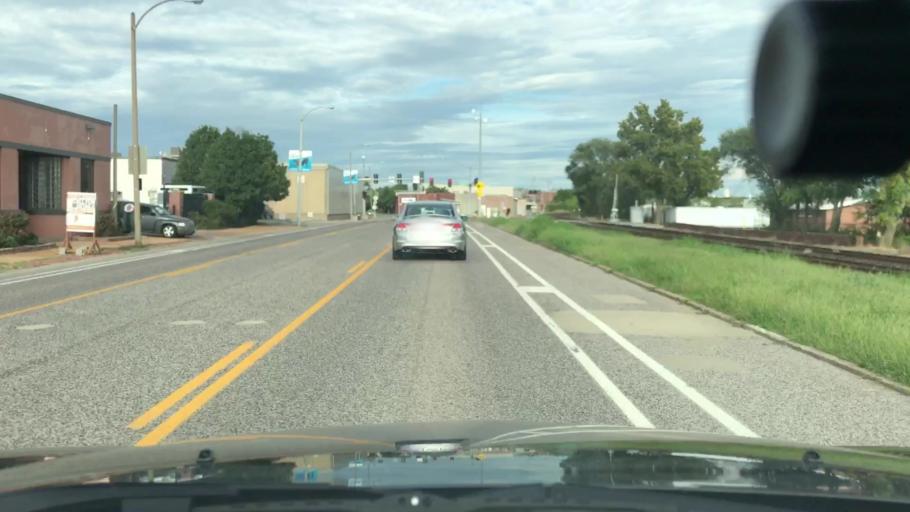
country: US
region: Missouri
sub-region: Saint Louis County
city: Richmond Heights
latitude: 38.6241
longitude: -90.2739
